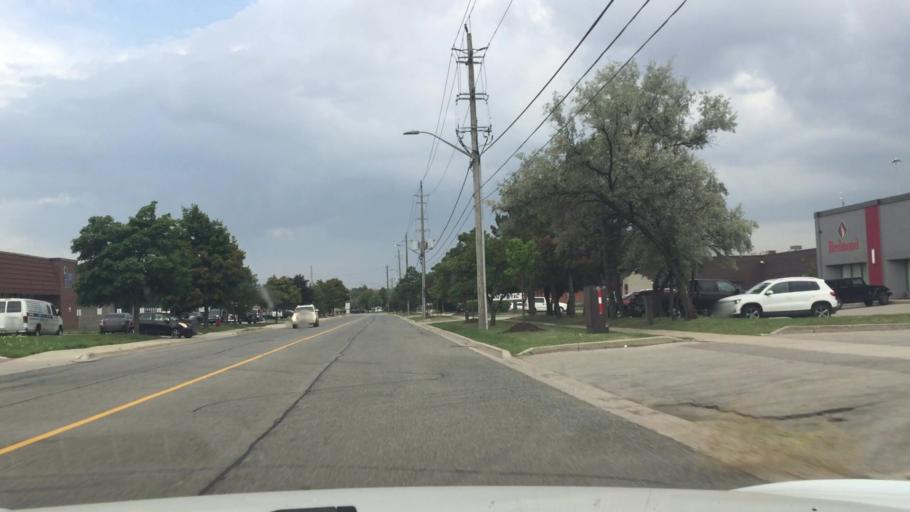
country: CA
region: Ontario
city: Mississauga
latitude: 43.6273
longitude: -79.6401
